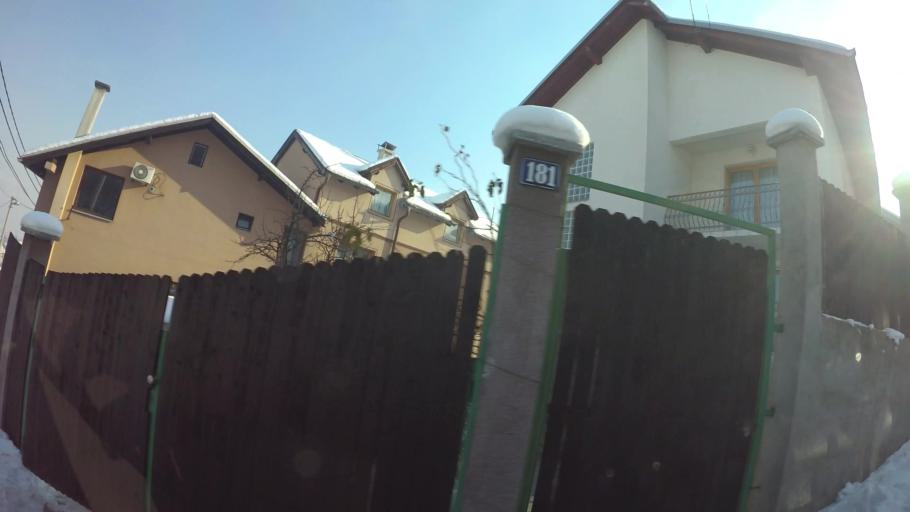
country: BA
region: Federation of Bosnia and Herzegovina
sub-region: Kanton Sarajevo
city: Sarajevo
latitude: 43.8431
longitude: 18.3771
